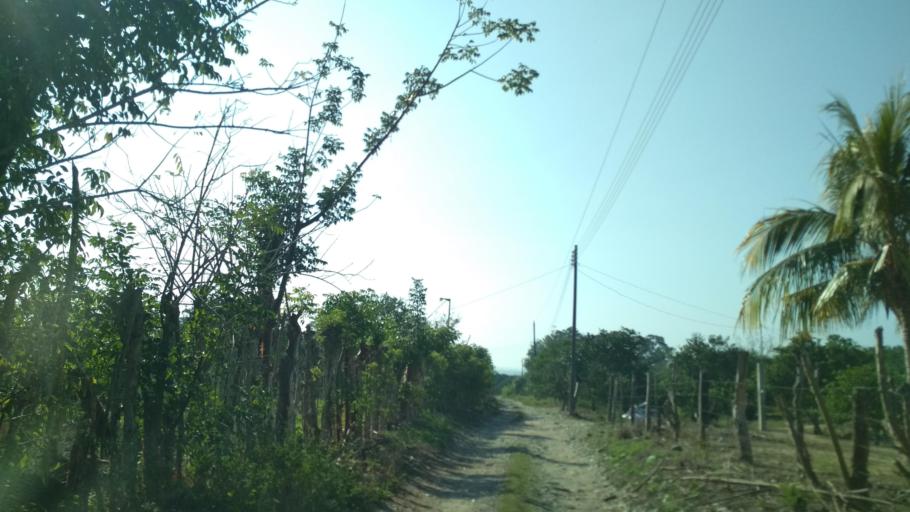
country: MX
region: Veracruz
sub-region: Papantla
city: Polutla
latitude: 20.4601
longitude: -97.2082
